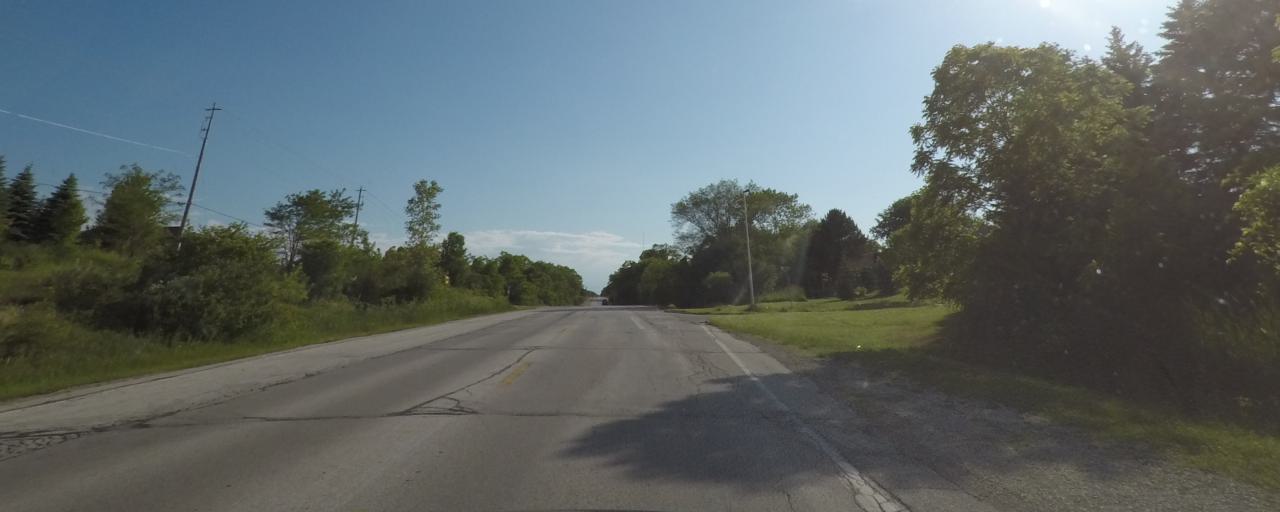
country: US
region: Wisconsin
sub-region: Milwaukee County
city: Hales Corners
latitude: 42.9707
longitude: -88.0565
